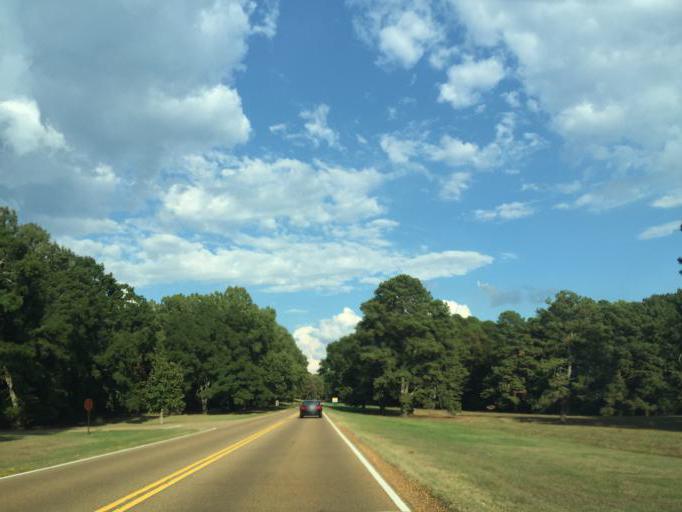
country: US
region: Mississippi
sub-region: Madison County
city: Ridgeland
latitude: 32.4266
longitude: -90.1254
